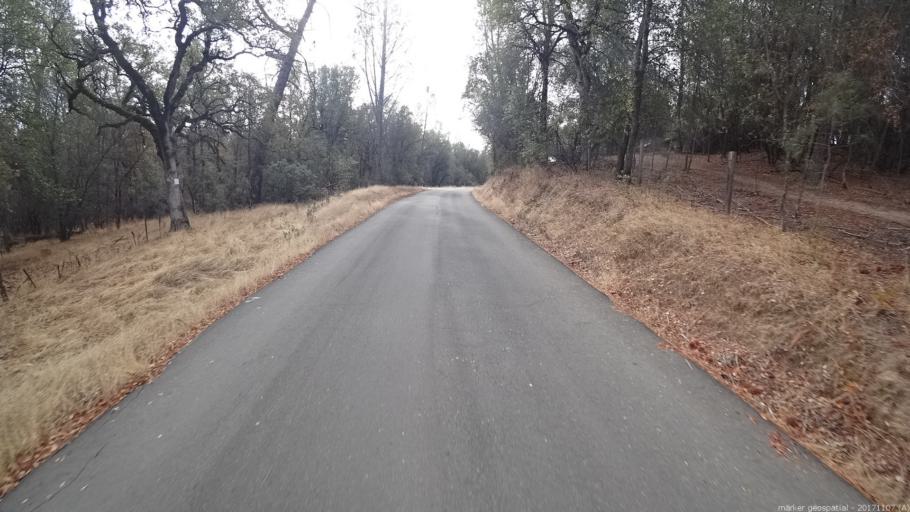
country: US
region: California
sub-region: Shasta County
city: Shasta
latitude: 40.5036
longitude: -122.5718
